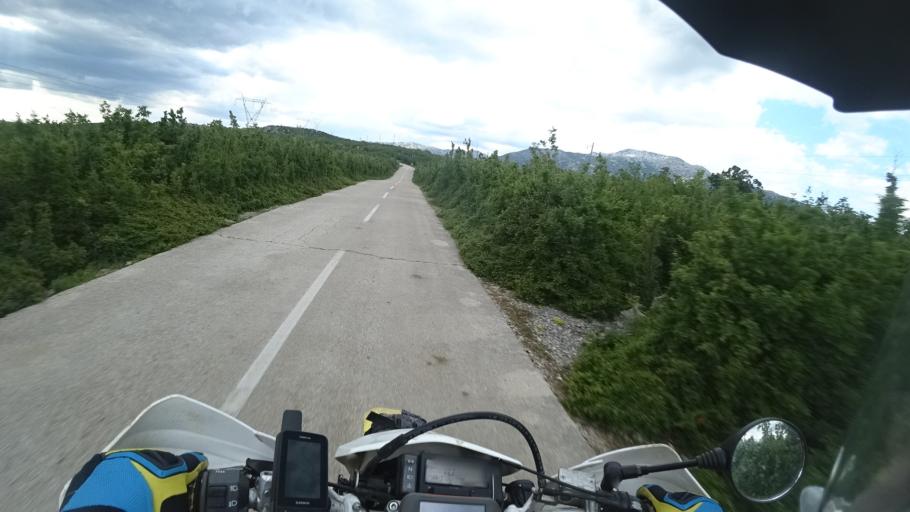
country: HR
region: Zadarska
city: Gracac
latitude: 44.2011
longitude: 15.8635
